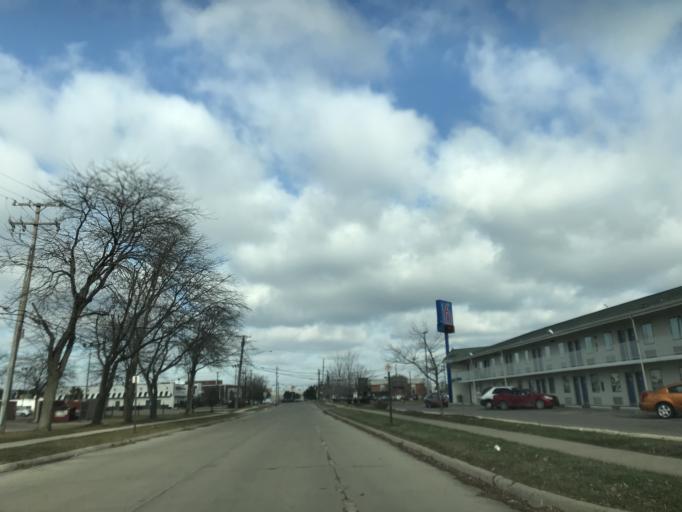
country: US
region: Michigan
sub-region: Oakland County
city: Clawson
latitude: 42.5317
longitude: -83.1116
